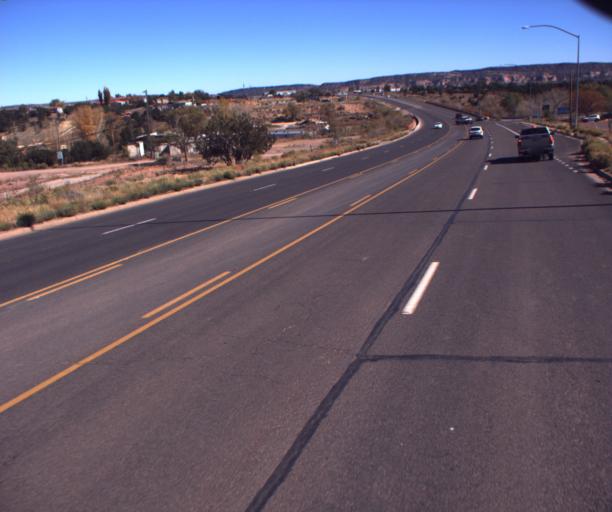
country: US
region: Arizona
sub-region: Apache County
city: Saint Michaels
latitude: 35.6558
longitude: -109.1070
